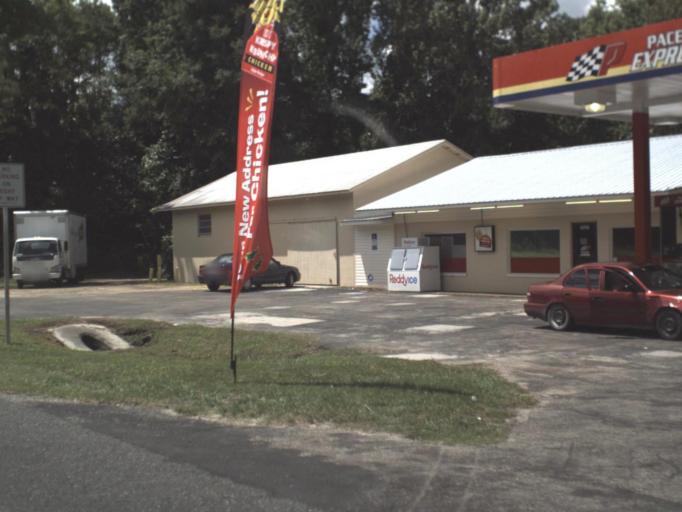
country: US
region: Florida
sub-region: Taylor County
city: Perry
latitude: 30.3002
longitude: -83.7455
